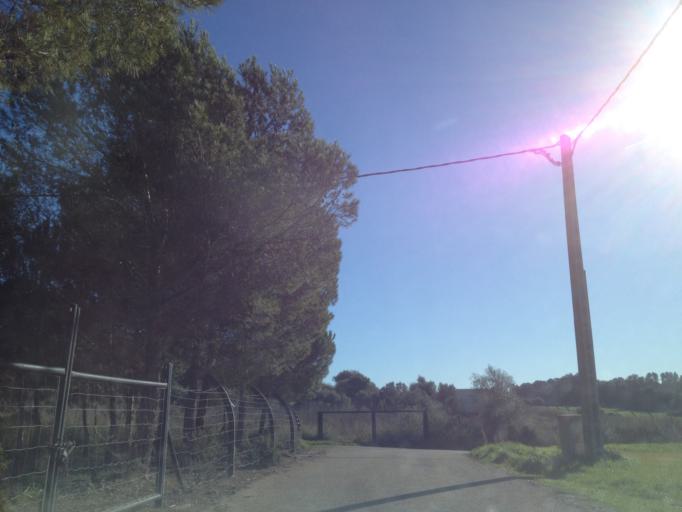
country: ES
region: Balearic Islands
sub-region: Illes Balears
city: Sineu
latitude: 39.6522
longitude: 3.0380
